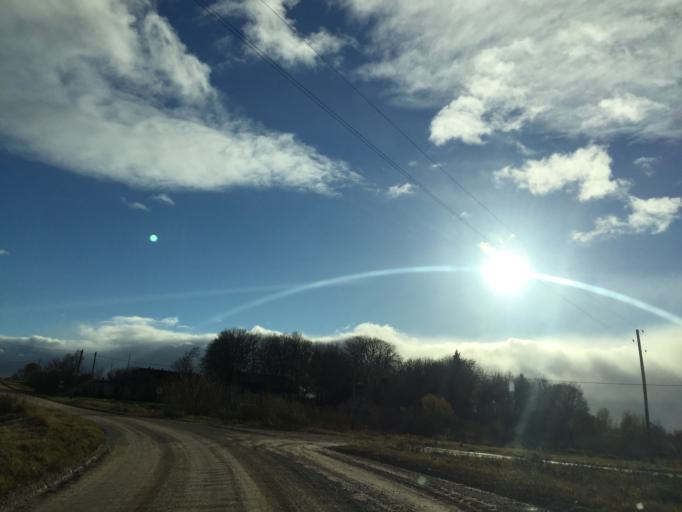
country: LV
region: Tukuma Rajons
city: Tukums
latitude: 56.9708
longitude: 22.9612
